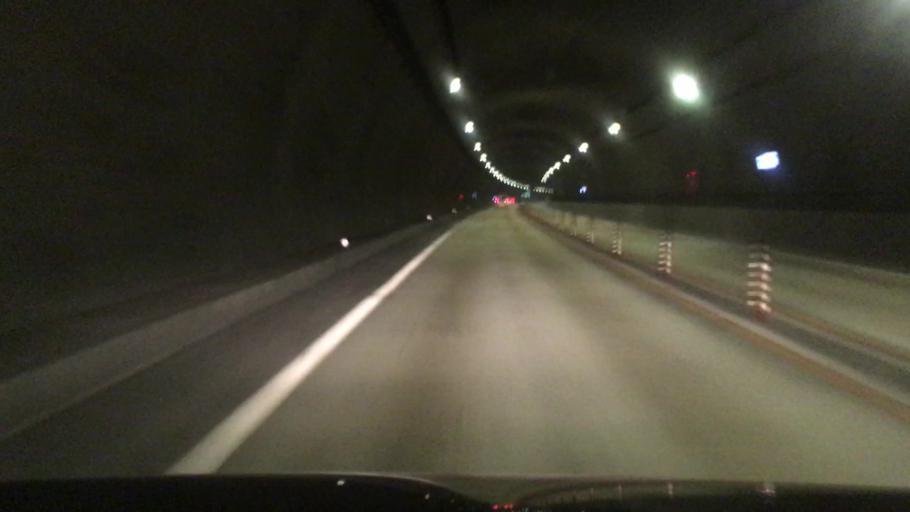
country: JP
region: Hyogo
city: Toyooka
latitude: 35.3676
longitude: 134.7577
